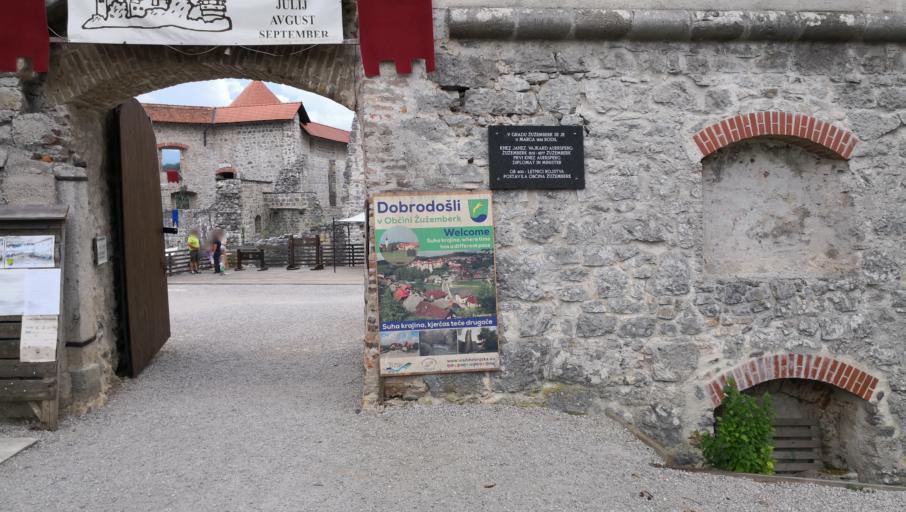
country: SI
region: Zuzemberk
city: Zuzemberk
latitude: 45.8305
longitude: 14.9289
